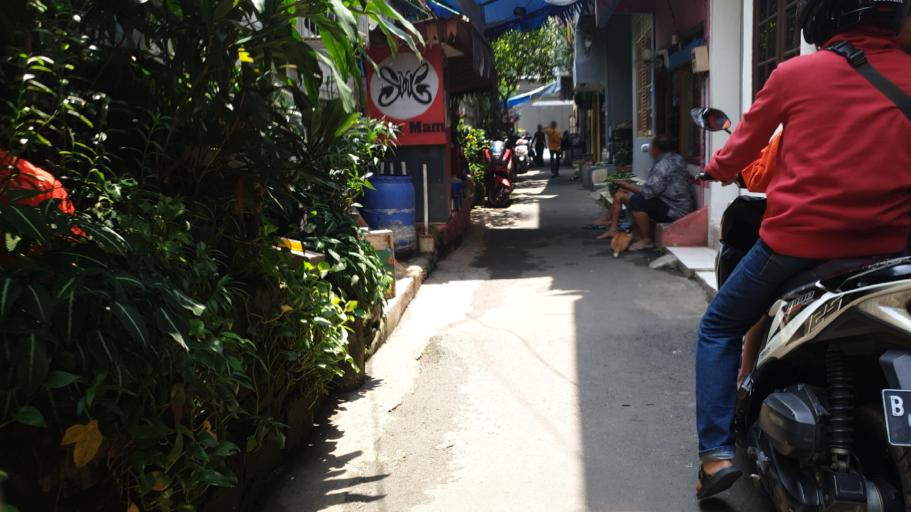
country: ID
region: Jakarta Raya
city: Jakarta
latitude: -6.2595
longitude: 106.7944
